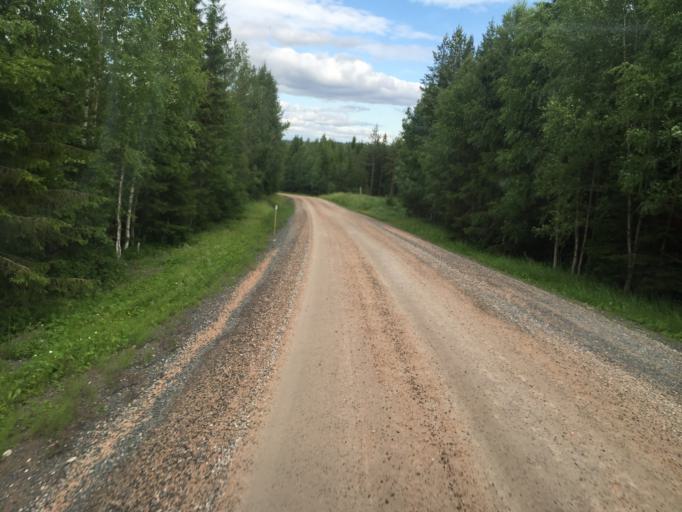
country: SE
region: Dalarna
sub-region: Malung-Saelens kommun
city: Malung
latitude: 60.8990
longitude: 13.7328
